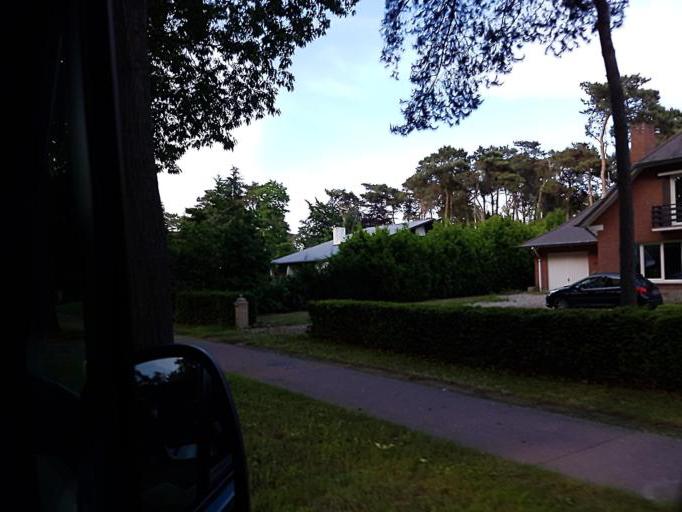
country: BE
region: Flanders
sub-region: Provincie Limburg
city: Lommel
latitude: 51.2422
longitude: 5.3092
